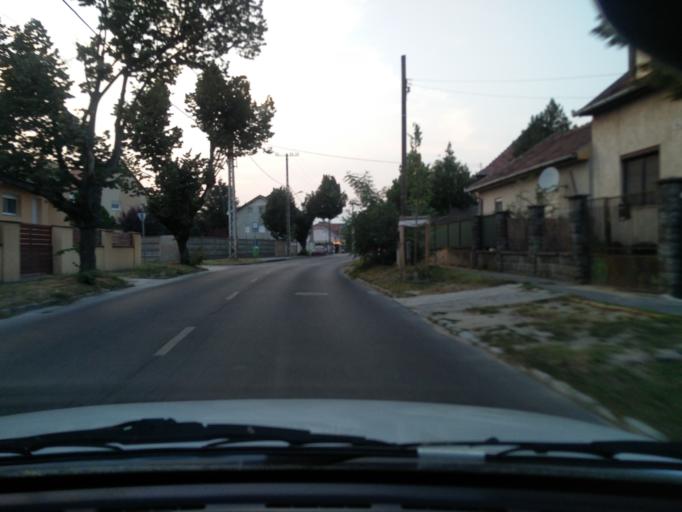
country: HU
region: Budapest
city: Budapest XXIII. keruelet
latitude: 47.3969
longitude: 19.0994
